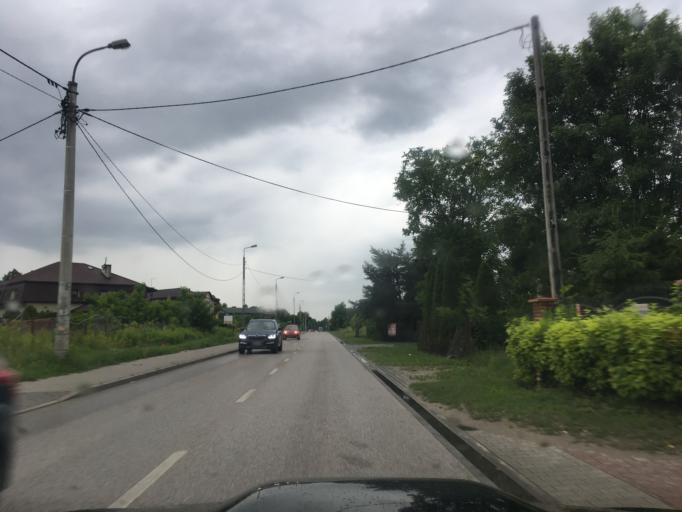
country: PL
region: Masovian Voivodeship
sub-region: Powiat piaseczynski
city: Zalesie Gorne
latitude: 52.0396
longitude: 21.0103
